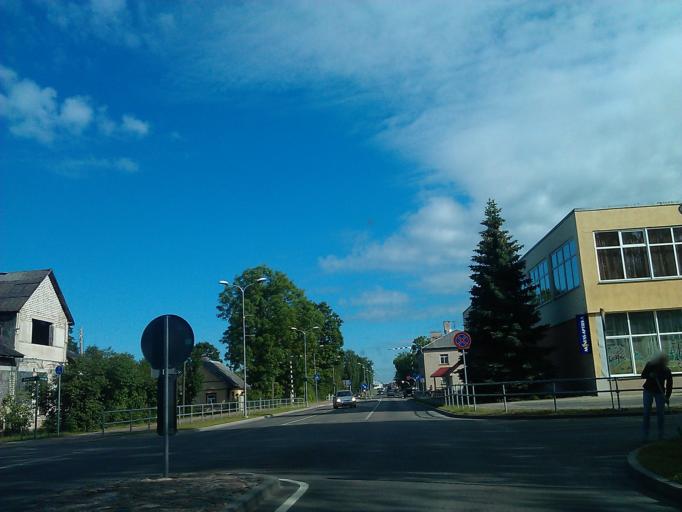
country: LV
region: Vilanu
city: Vilani
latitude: 56.5454
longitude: 26.9253
